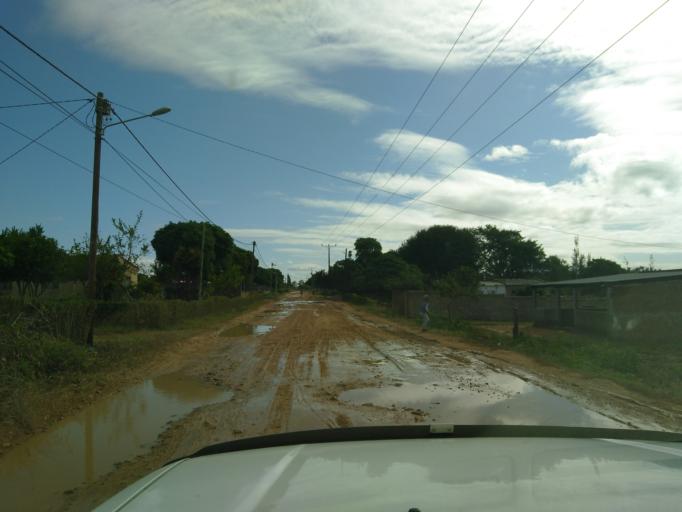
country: MZ
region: Maputo City
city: Maputo
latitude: -25.9973
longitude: 32.5395
